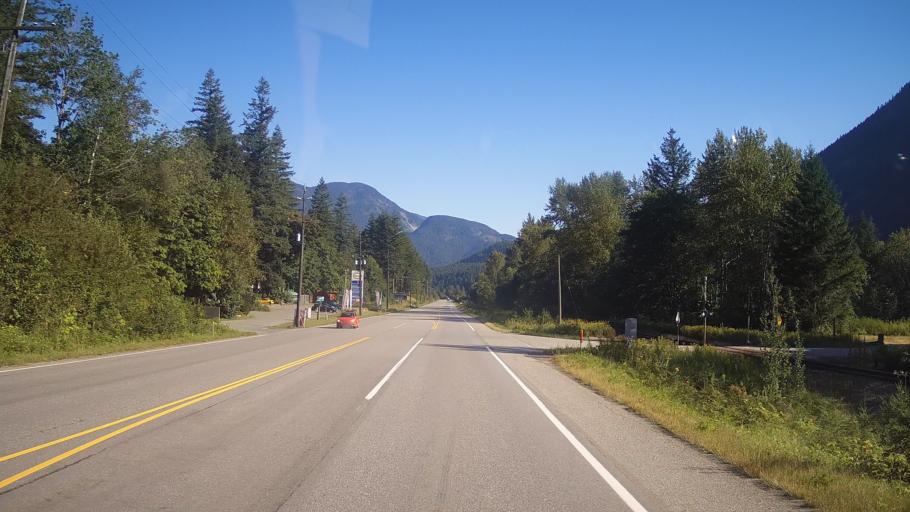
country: CA
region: British Columbia
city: Hope
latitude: 49.5181
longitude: -121.4204
